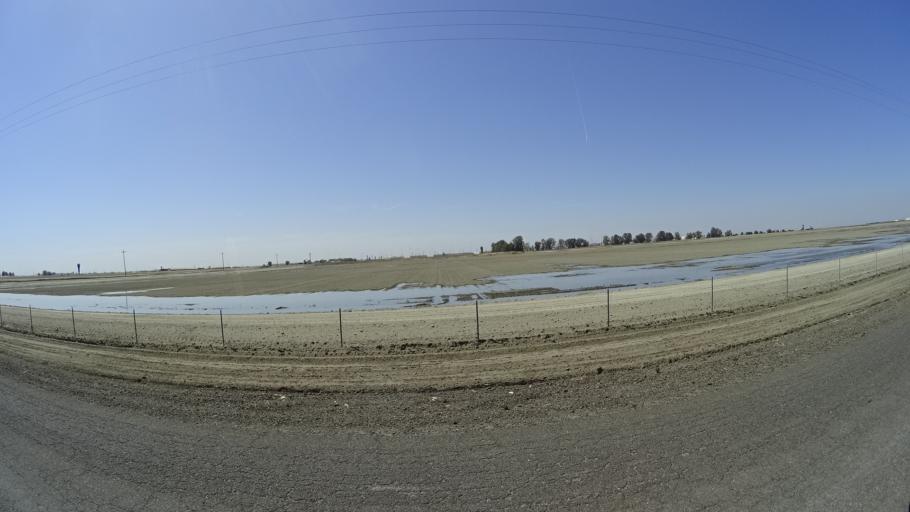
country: US
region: California
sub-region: Kings County
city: Corcoran
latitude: 36.0727
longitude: -119.5465
